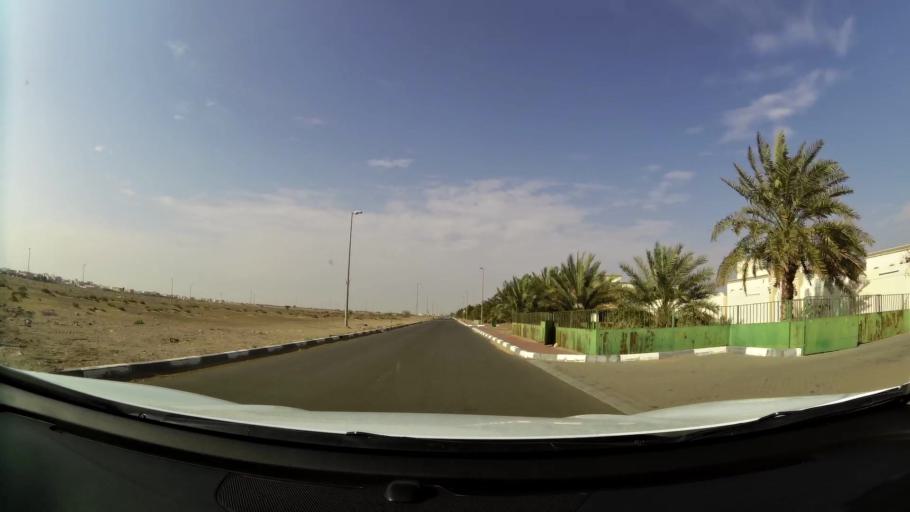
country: AE
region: Abu Dhabi
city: Al Ain
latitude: 24.0710
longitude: 55.8609
